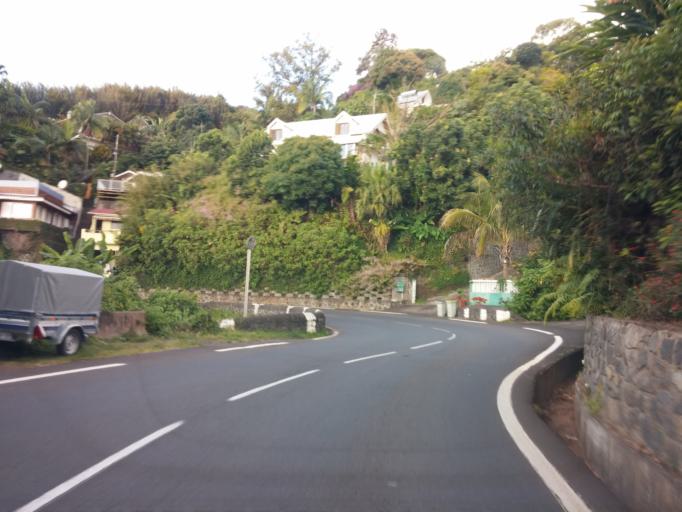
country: RE
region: Reunion
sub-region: Reunion
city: Saint-Denis
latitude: -20.8967
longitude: 55.4178
